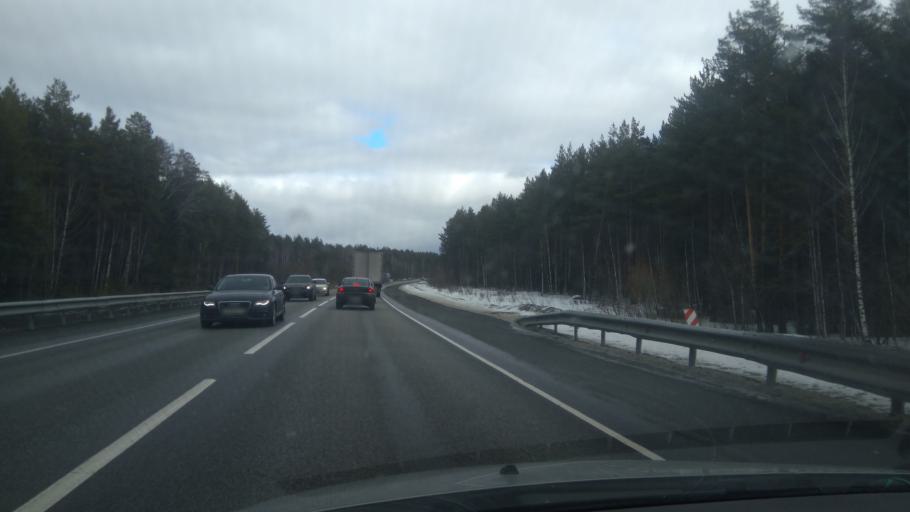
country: RU
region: Sverdlovsk
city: Bisert'
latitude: 56.8290
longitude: 58.7749
